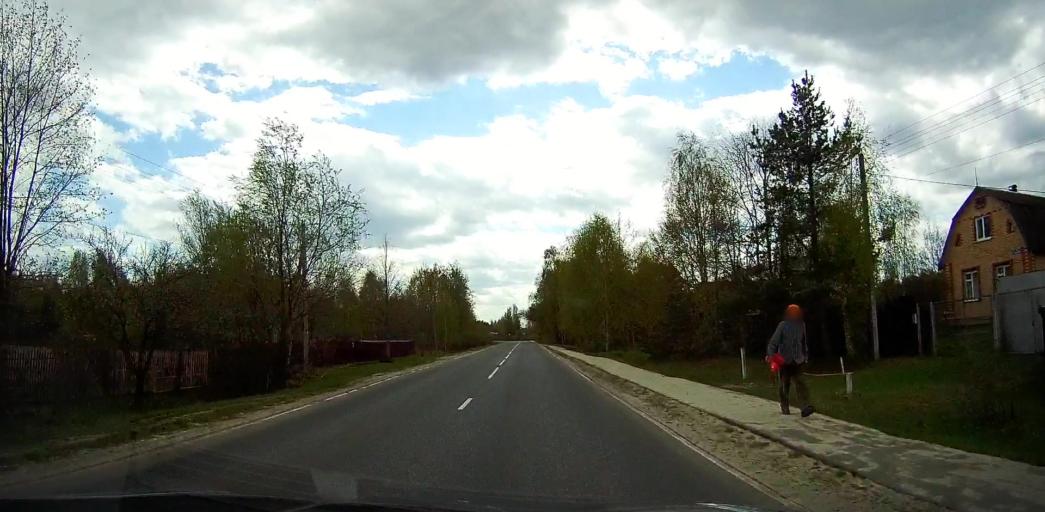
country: RU
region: Moskovskaya
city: Davydovo
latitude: 55.6623
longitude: 38.7563
